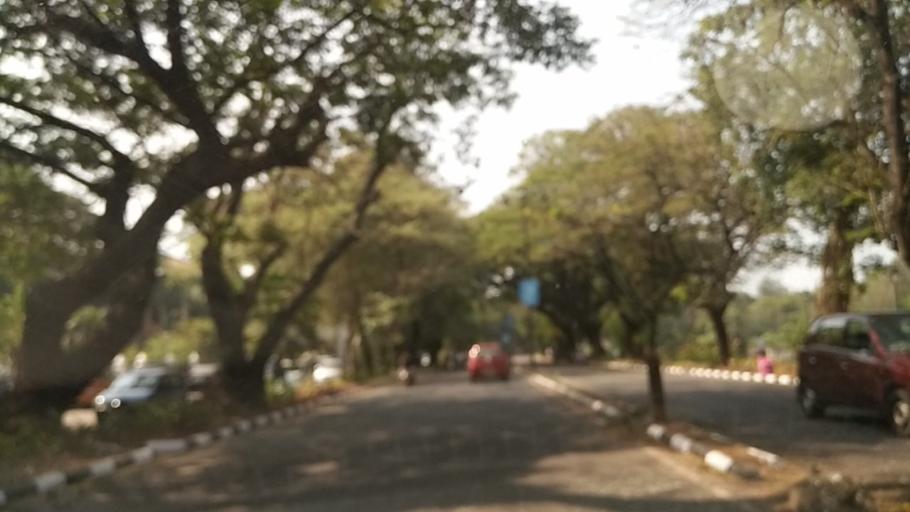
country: IN
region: Goa
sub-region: North Goa
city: Panaji
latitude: 15.5001
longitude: 73.8212
